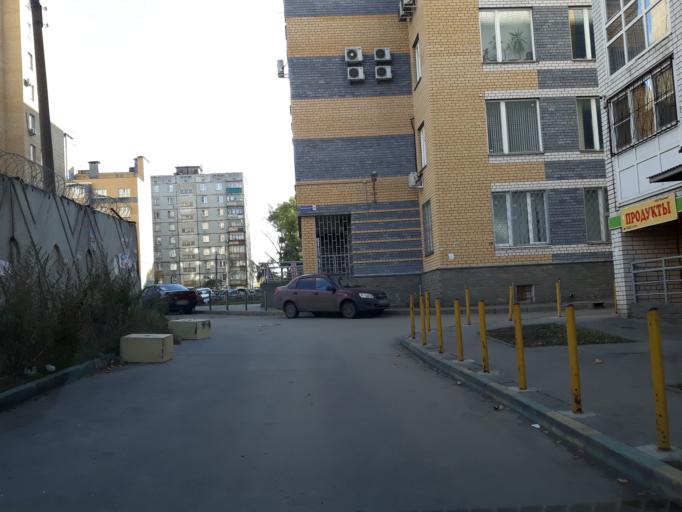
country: RU
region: Nizjnij Novgorod
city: Nizhniy Novgorod
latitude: 56.3043
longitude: 43.9357
